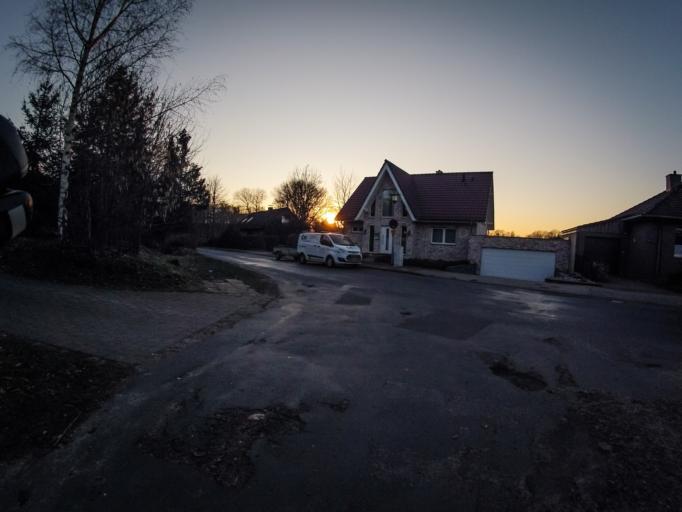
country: DE
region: North Rhine-Westphalia
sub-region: Regierungsbezirk Munster
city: Lotte
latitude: 52.3110
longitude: 7.9447
